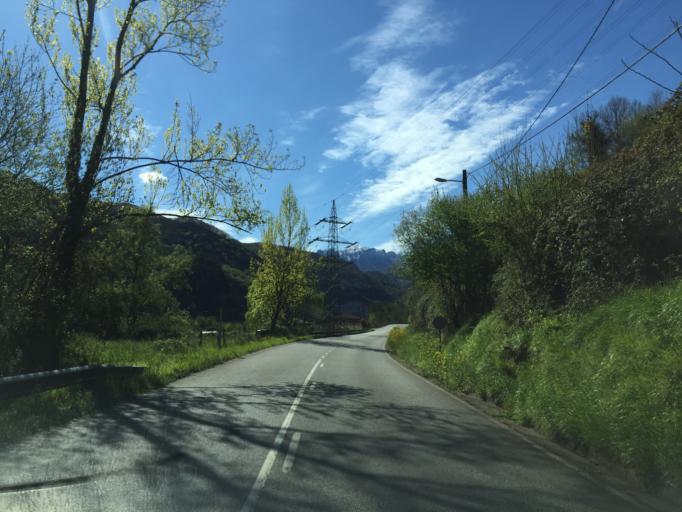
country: ES
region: Asturias
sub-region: Province of Asturias
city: Proaza
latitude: 43.3199
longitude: -5.9926
